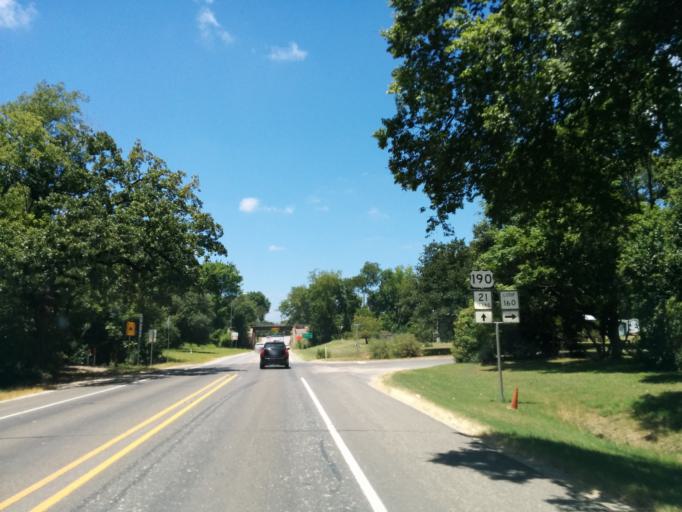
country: US
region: Texas
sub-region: Leon County
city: Hilltop Lakes
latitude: 30.9142
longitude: -96.1088
